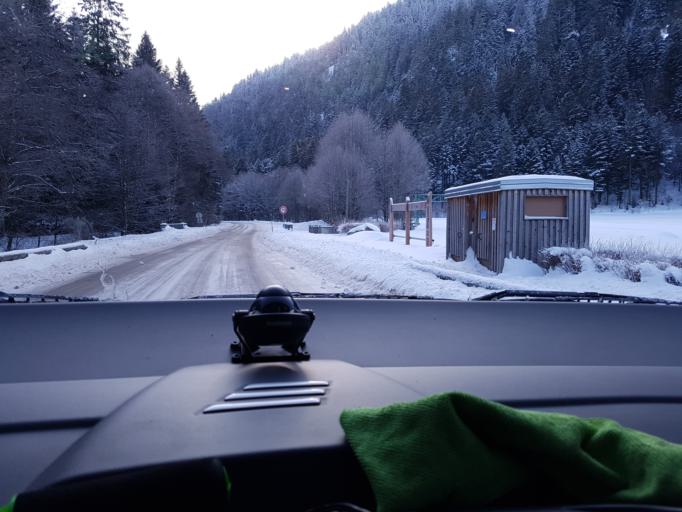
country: FR
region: Lorraine
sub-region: Departement des Vosges
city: Xonrupt-Longemer
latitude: 48.0633
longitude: 6.9603
